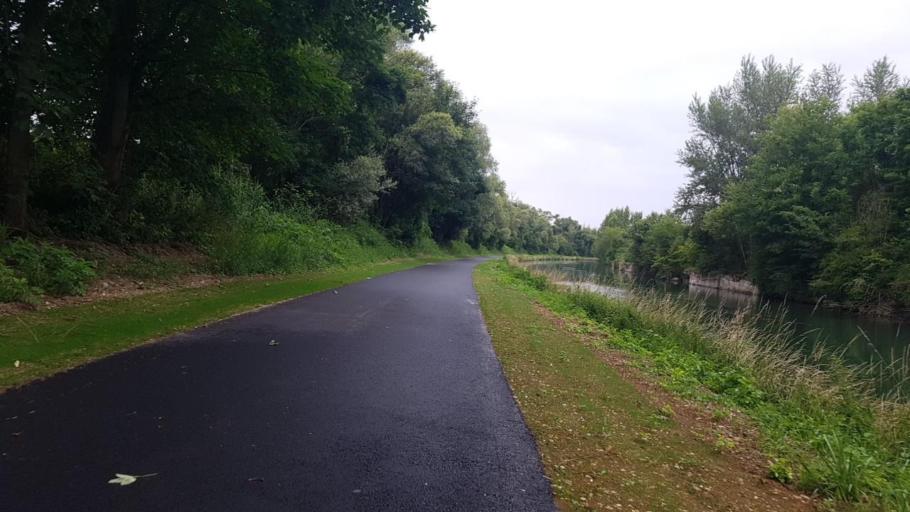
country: FR
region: Champagne-Ardenne
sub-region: Departement de la Marne
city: Vitry-le-Francois
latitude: 48.7757
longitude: 4.5439
